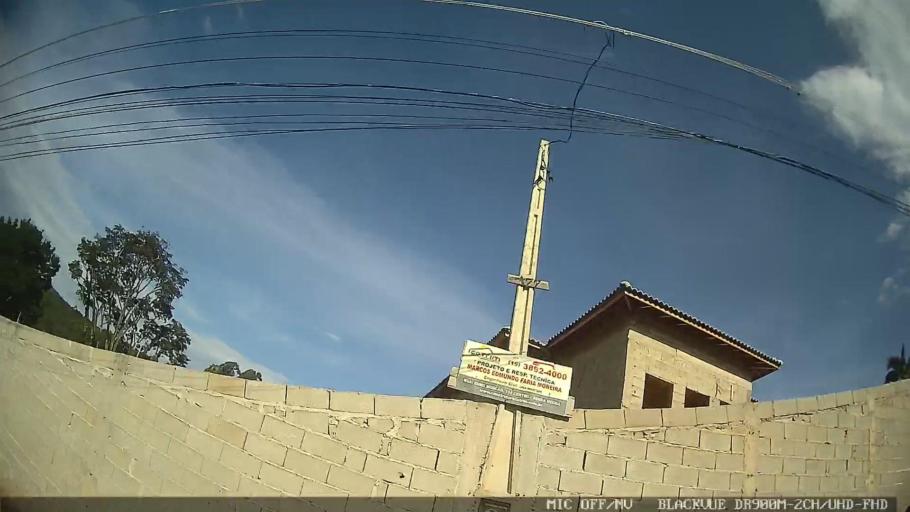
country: BR
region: Sao Paulo
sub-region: Serra Negra
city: Serra Negra
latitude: -22.6371
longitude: -46.6993
